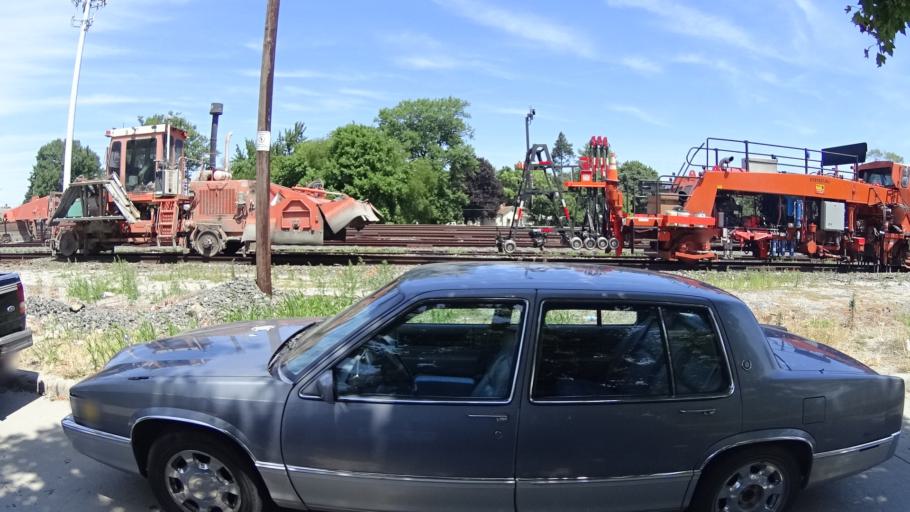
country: US
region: Ohio
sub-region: Erie County
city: Sandusky
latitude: 41.4399
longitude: -82.7167
